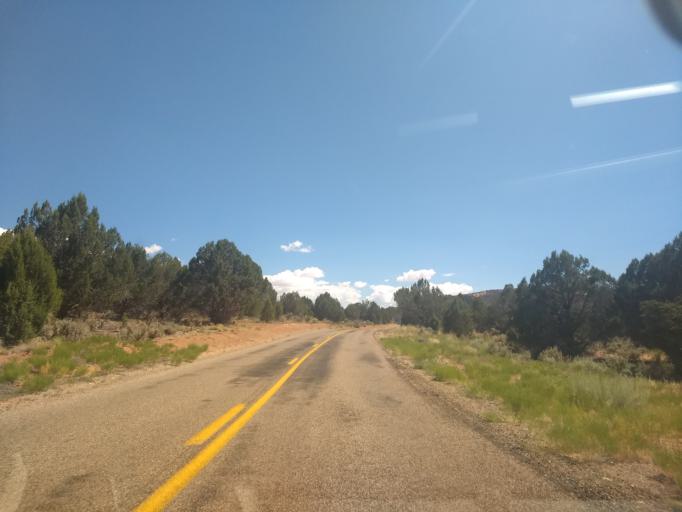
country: US
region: Utah
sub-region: Washington County
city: Hildale
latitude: 36.9946
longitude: -112.8641
